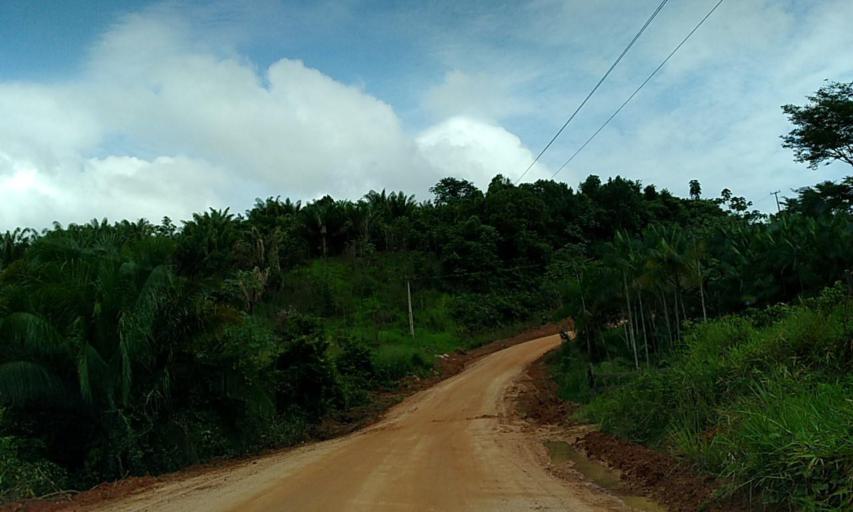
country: BR
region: Para
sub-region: Senador Jose Porfirio
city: Senador Jose Porfirio
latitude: -3.0771
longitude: -51.6352
